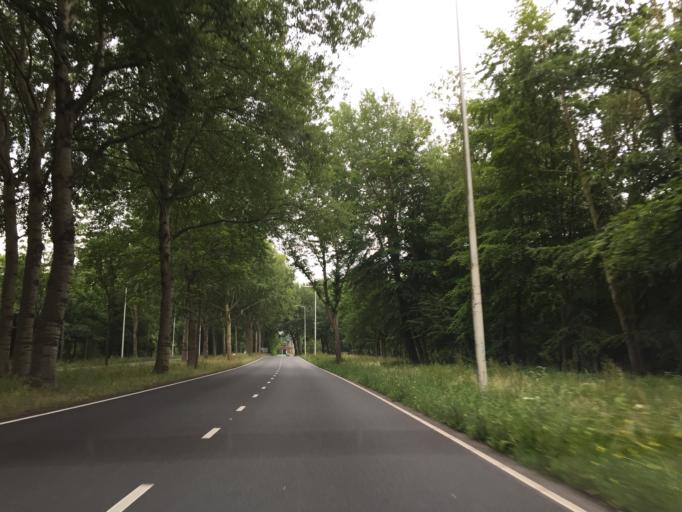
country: NL
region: South Holland
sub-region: Gemeente Westland
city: Poeldijk
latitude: 52.0493
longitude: 4.2309
